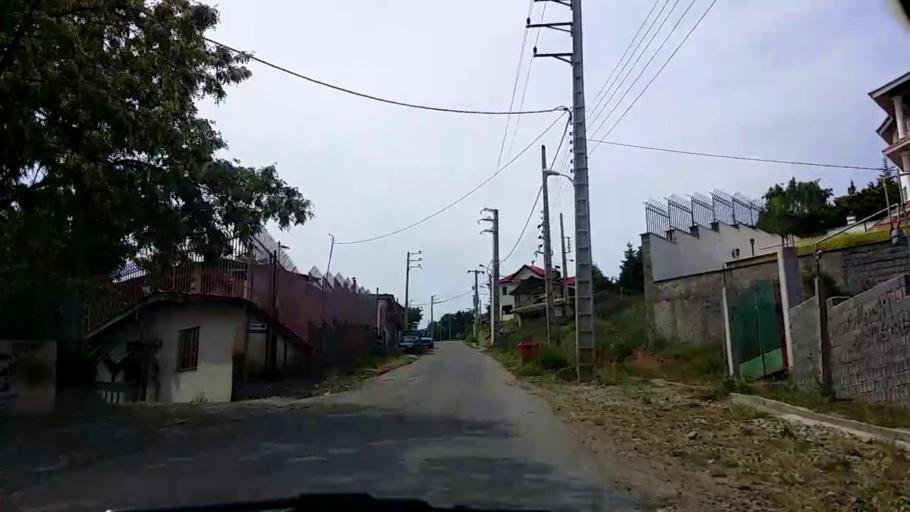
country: IR
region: Mazandaran
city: `Abbasabad
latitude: 36.5499
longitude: 51.1844
